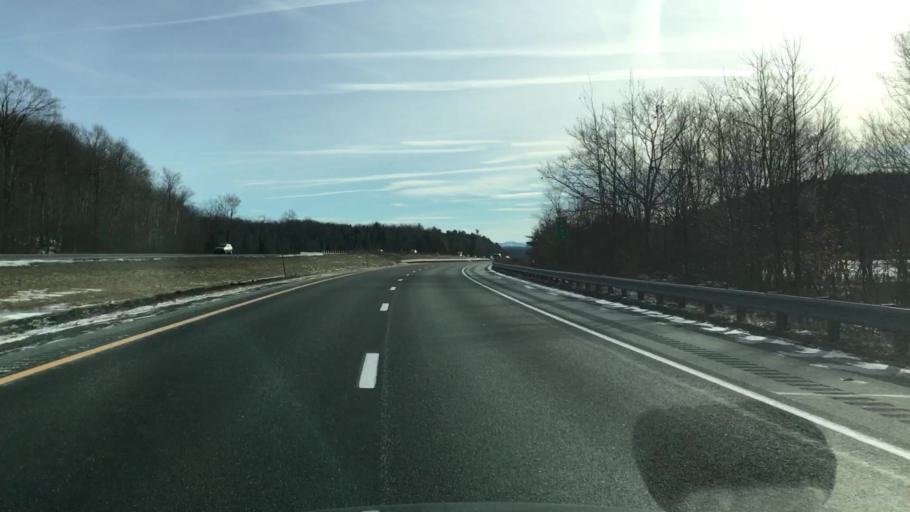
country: US
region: New Hampshire
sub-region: Sullivan County
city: Grantham
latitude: 43.5608
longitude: -72.1429
